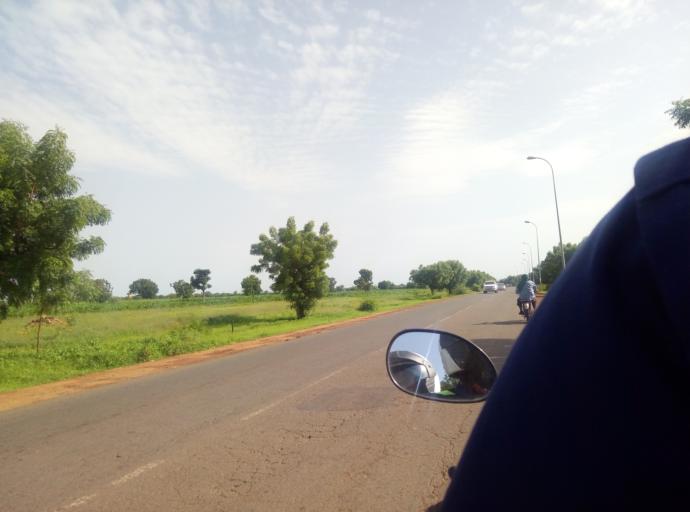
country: ML
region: Bamako
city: Bamako
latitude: 12.5521
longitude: -7.9492
